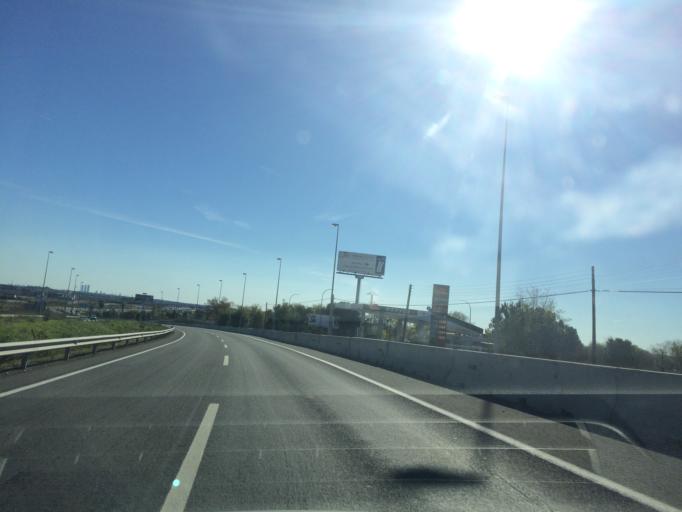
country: ES
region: Madrid
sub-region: Provincia de Madrid
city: Colmenar Viejo
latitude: 40.6403
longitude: -3.7315
